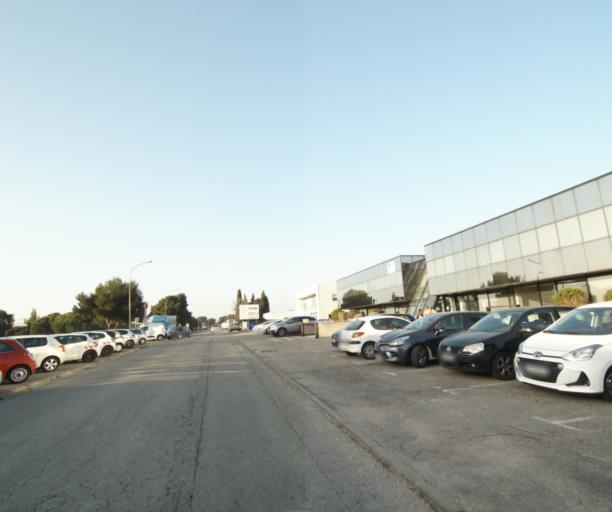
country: FR
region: Provence-Alpes-Cote d'Azur
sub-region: Departement des Bouches-du-Rhone
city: Saint-Victoret
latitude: 43.4347
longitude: 5.2397
